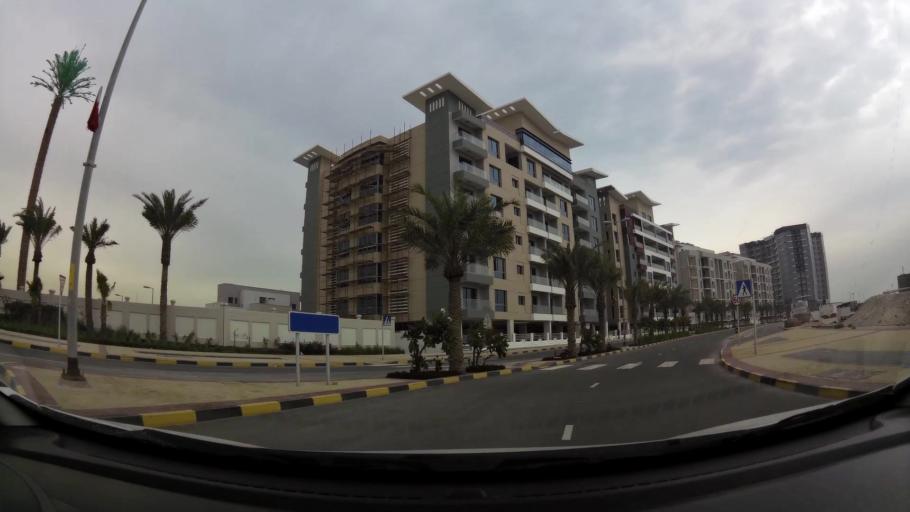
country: BH
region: Central Governorate
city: Dar Kulayb
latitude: 25.8682
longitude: 50.6074
